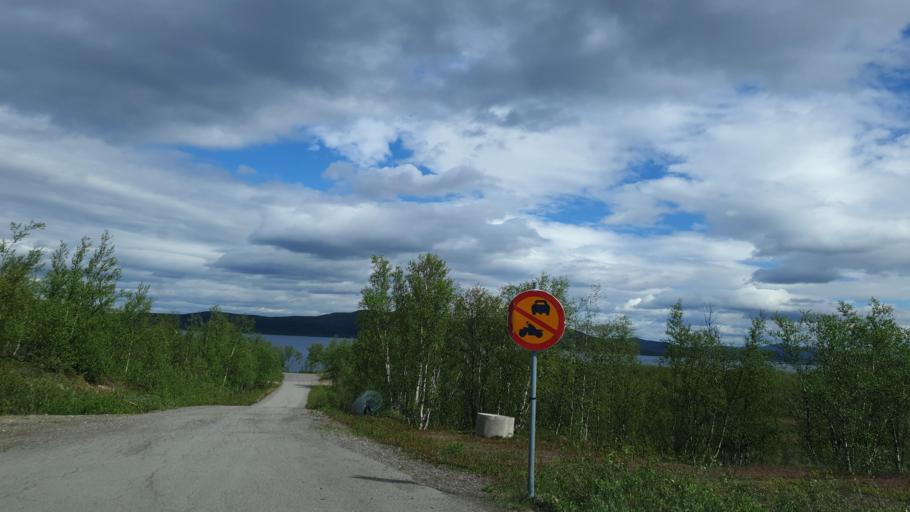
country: SE
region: Norrbotten
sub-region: Kiruna Kommun
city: Kiruna
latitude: 68.2261
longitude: 19.7204
